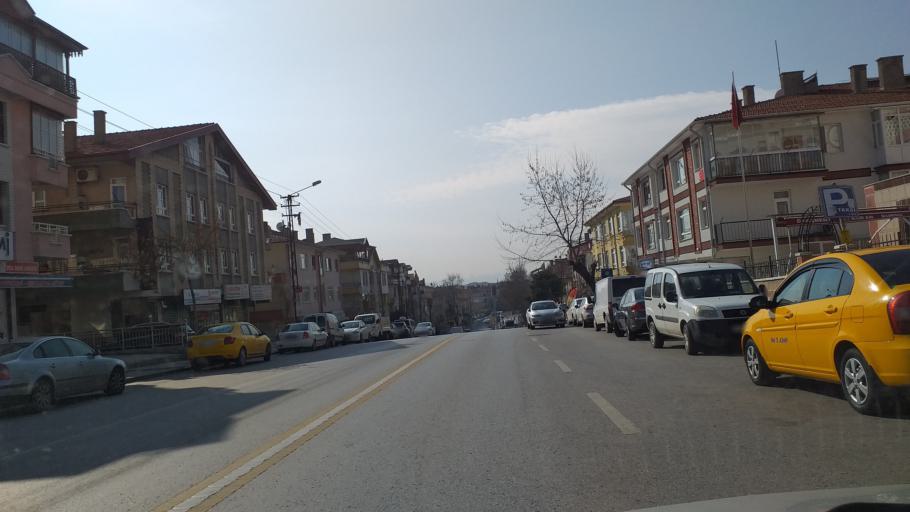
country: TR
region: Ankara
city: Ankara
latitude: 39.9867
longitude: 32.8543
